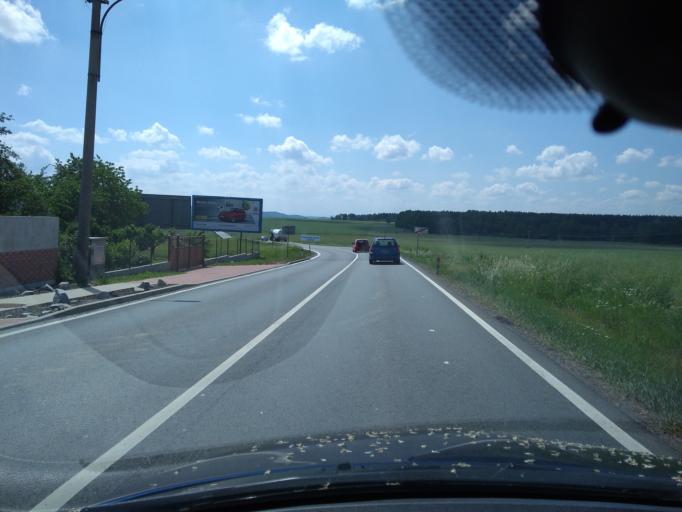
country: CZ
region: Plzensky
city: Chlumcany
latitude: 49.6096
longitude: 13.3242
